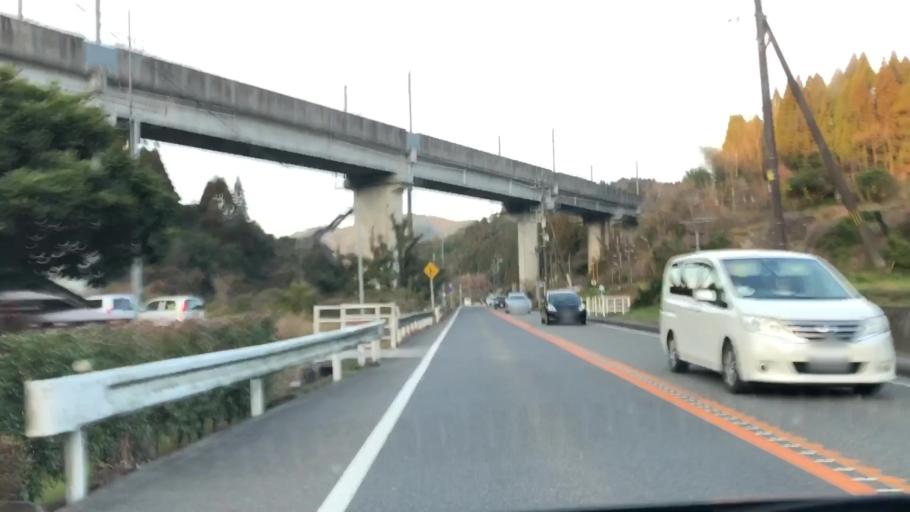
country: JP
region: Kumamoto
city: Minamata
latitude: 32.2169
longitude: 130.4374
